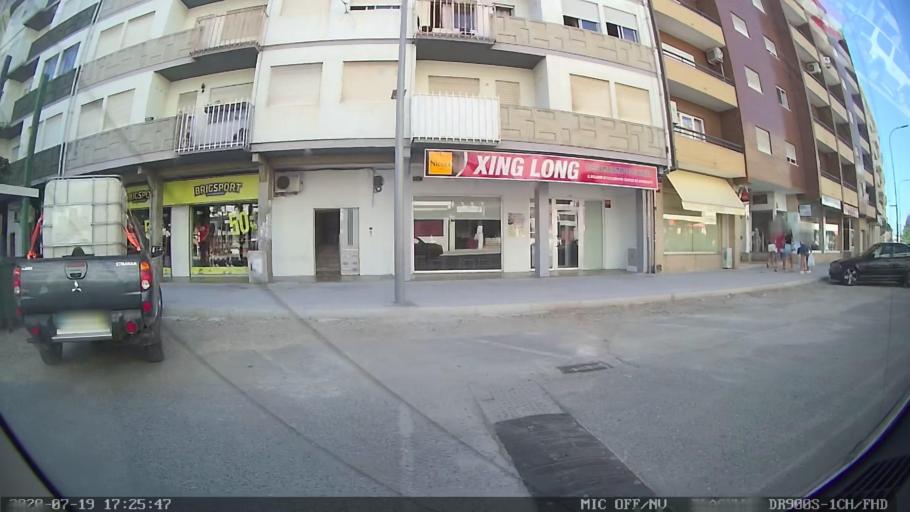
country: PT
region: Braganca
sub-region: Braganca Municipality
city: Braganca
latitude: 41.8028
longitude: -6.7608
